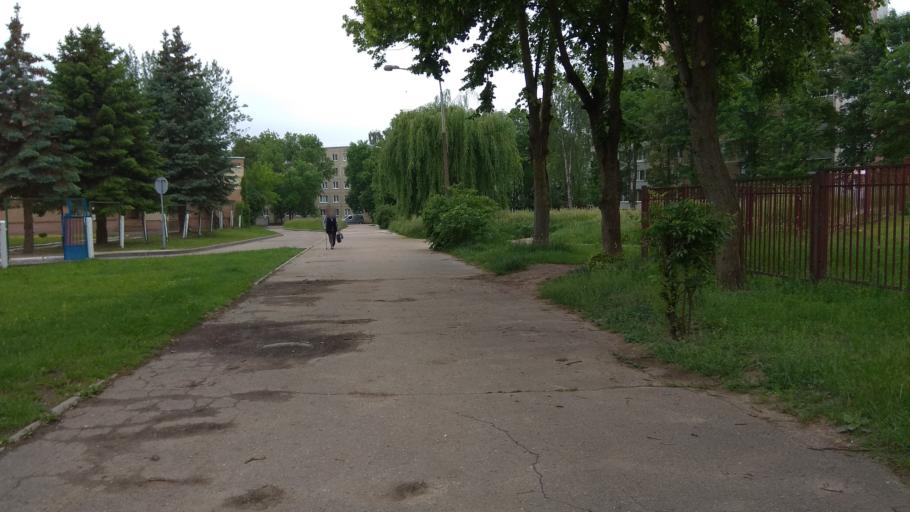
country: BY
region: Grodnenskaya
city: Hrodna
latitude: 53.7070
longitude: 23.8000
